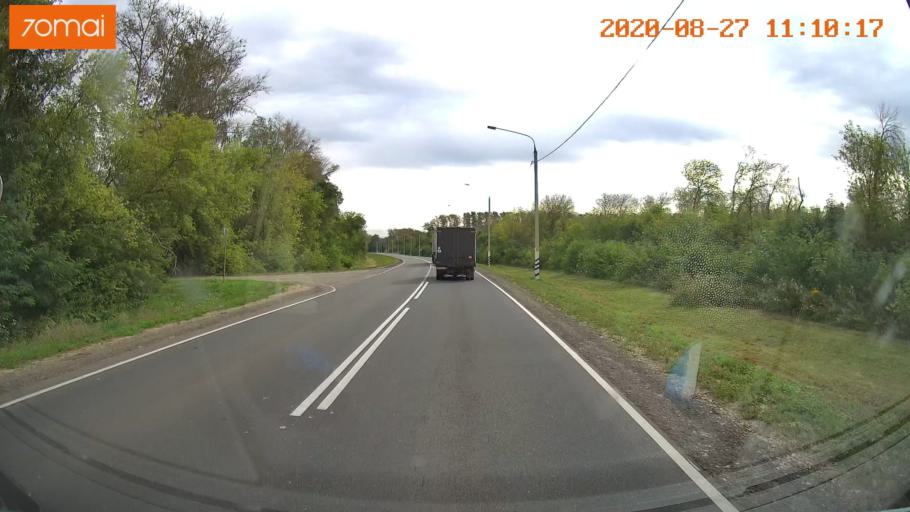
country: RU
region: Rjazan
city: Oktyabr'skiy
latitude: 54.1420
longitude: 38.7327
